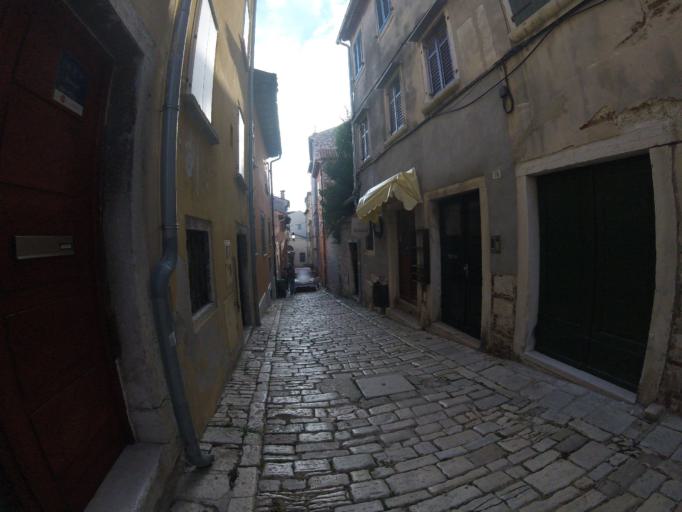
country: HR
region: Istarska
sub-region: Grad Rovinj
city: Rovinj
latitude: 45.0835
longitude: 13.6318
